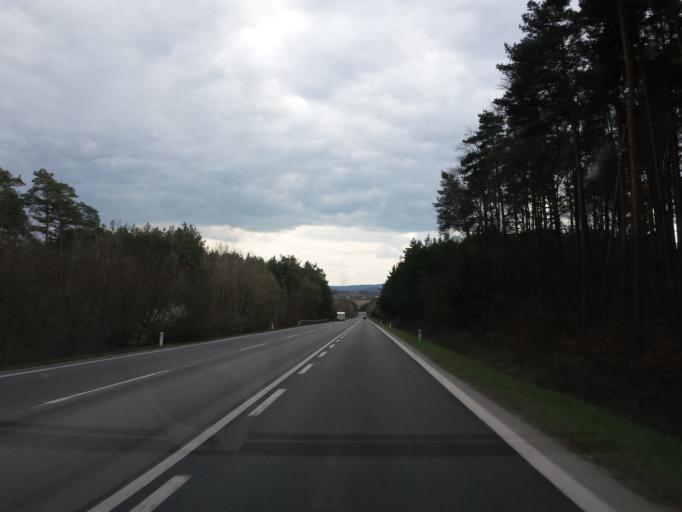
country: AT
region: Lower Austria
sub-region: Politischer Bezirk Krems
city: Lengenfeld
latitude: 48.4851
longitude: 15.5809
